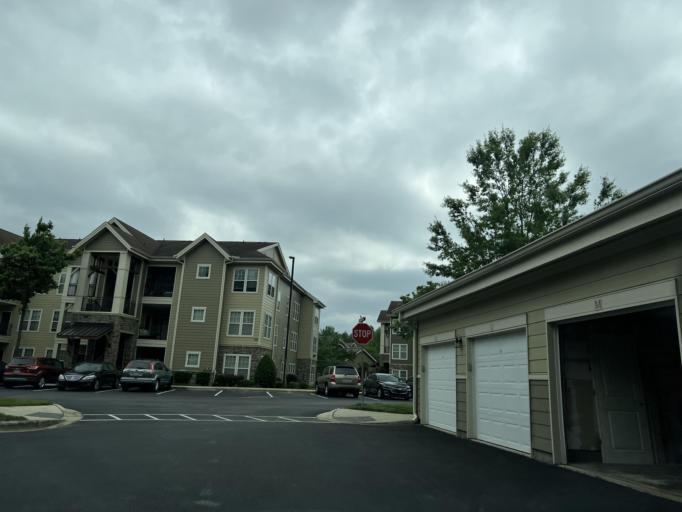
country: US
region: North Carolina
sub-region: Wake County
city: Raleigh
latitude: 35.8765
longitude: -78.5854
